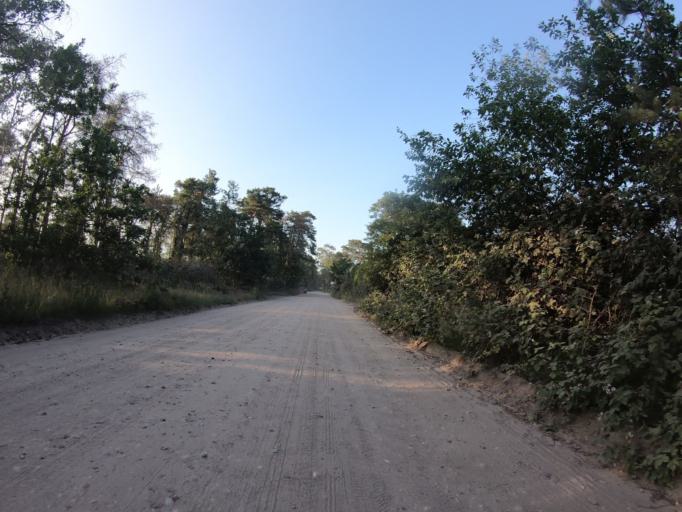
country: DE
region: Lower Saxony
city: Wagenhoff
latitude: 52.5355
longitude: 10.4927
